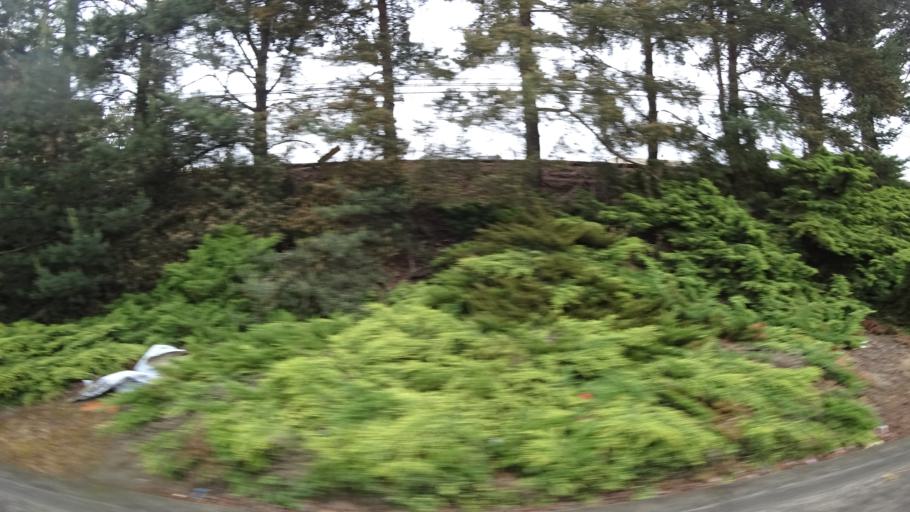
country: US
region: Oregon
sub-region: Washington County
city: Raleigh Hills
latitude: 45.4801
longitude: -122.7828
